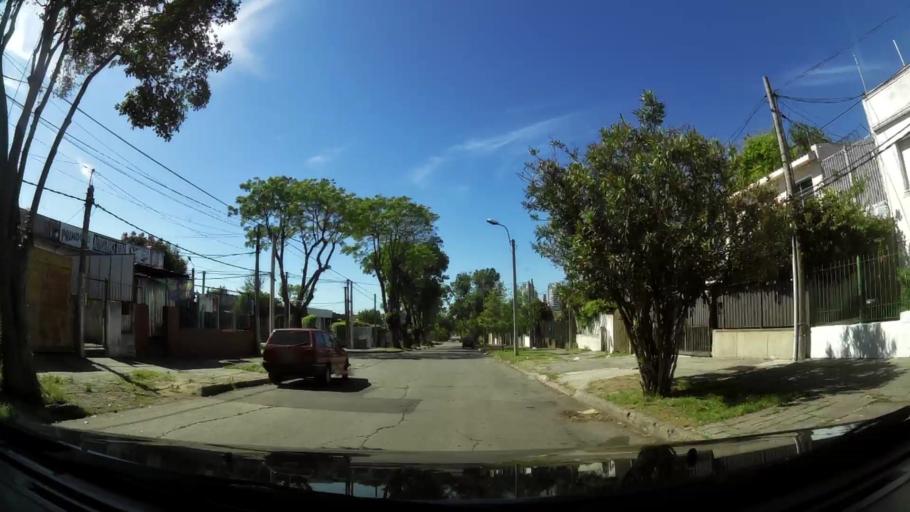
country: UY
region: Montevideo
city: Montevideo
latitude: -34.8899
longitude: -56.1232
